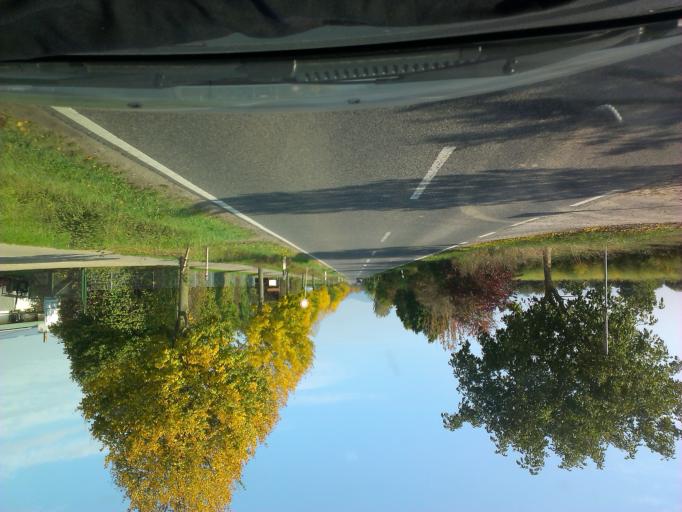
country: DE
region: Rheinland-Pfalz
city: Hassloch
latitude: 49.3750
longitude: 8.2497
